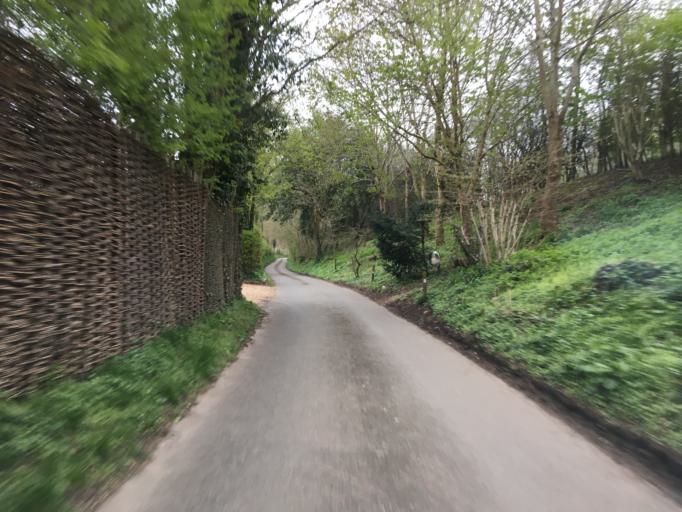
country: GB
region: England
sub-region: Gloucestershire
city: Wotton-under-Edge
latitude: 51.5988
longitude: -2.3064
